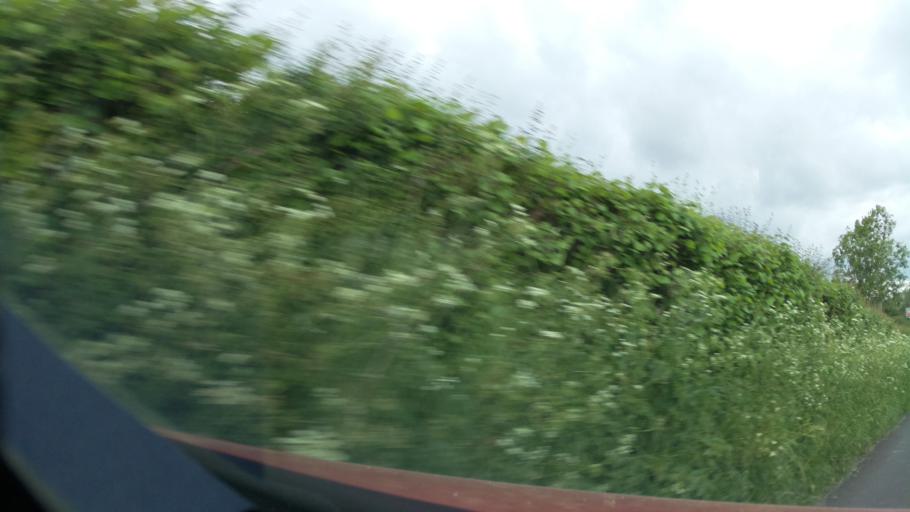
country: GB
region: England
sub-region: South Gloucestershire
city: Pucklechurch
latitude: 51.4665
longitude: -2.4245
